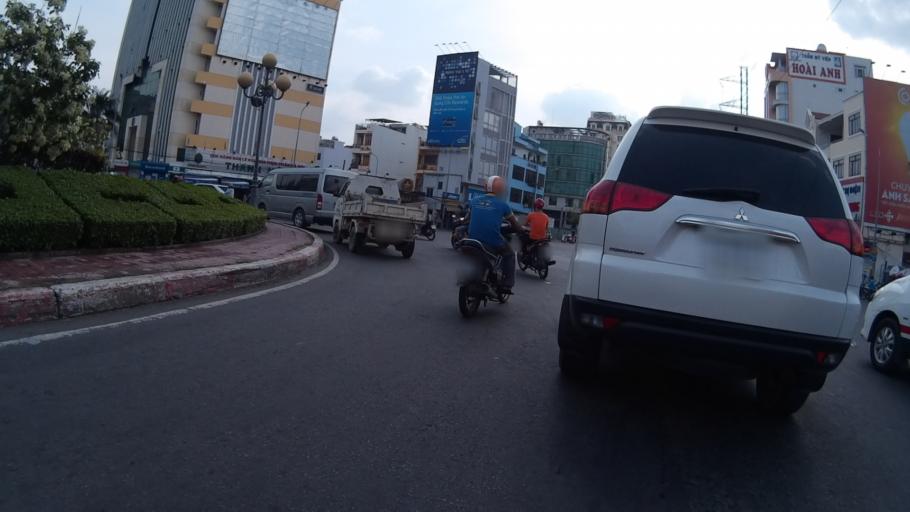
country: VN
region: Ho Chi Minh City
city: Quan Binh Thanh
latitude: 10.7925
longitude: 106.6992
